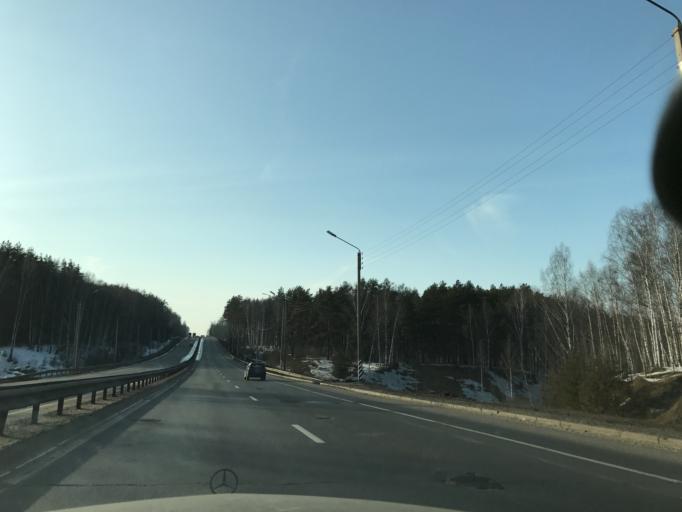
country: RU
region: Vladimir
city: Novovyazniki
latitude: 56.2199
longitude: 42.1772
